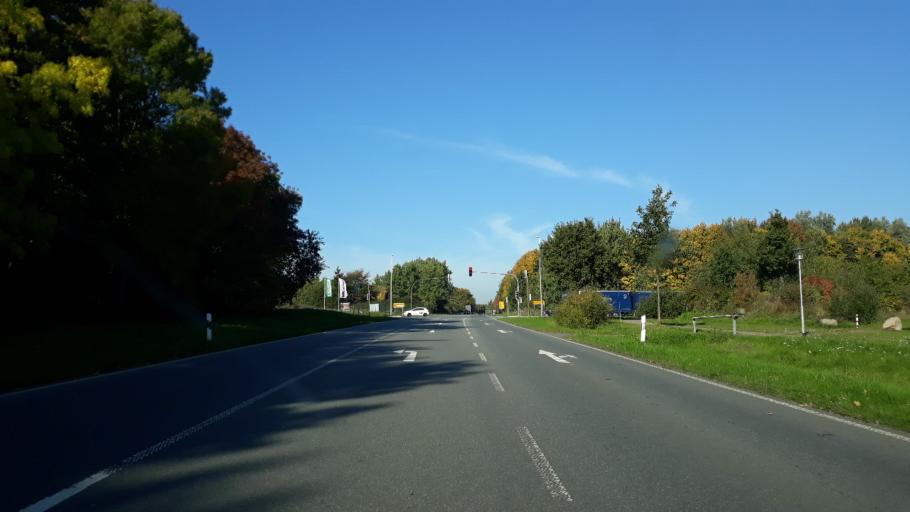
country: DE
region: Schleswig-Holstein
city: Schleswig
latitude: 54.5340
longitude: 9.5608
